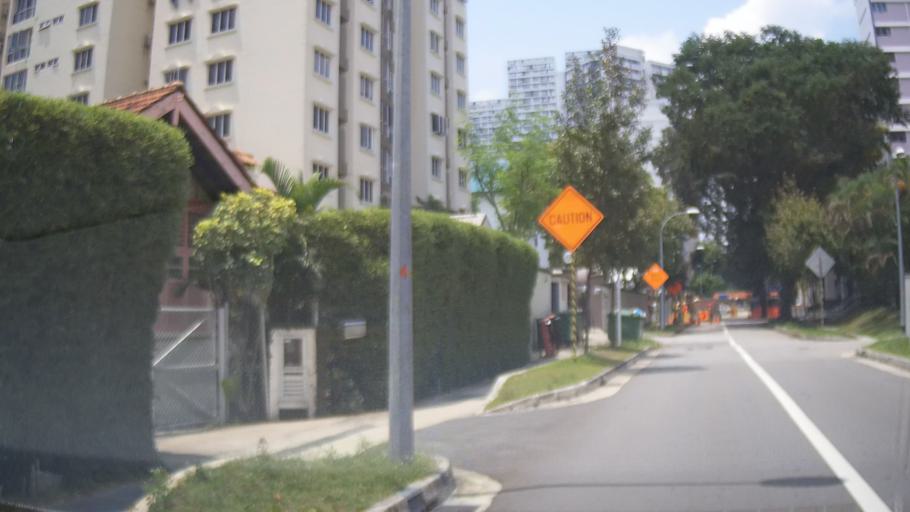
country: SG
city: Singapore
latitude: 1.3250
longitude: 103.8639
